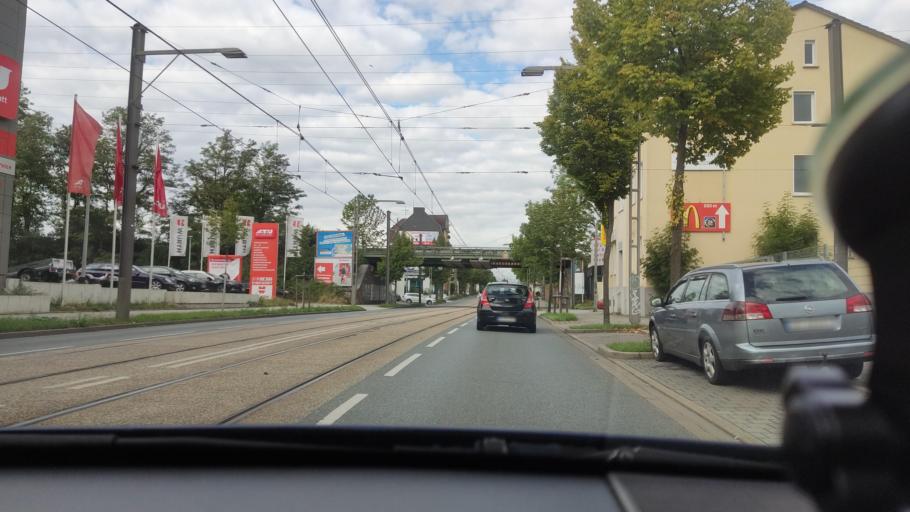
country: DE
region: North Rhine-Westphalia
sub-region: Regierungsbezirk Arnsberg
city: Dortmund
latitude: 51.5404
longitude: 7.4574
